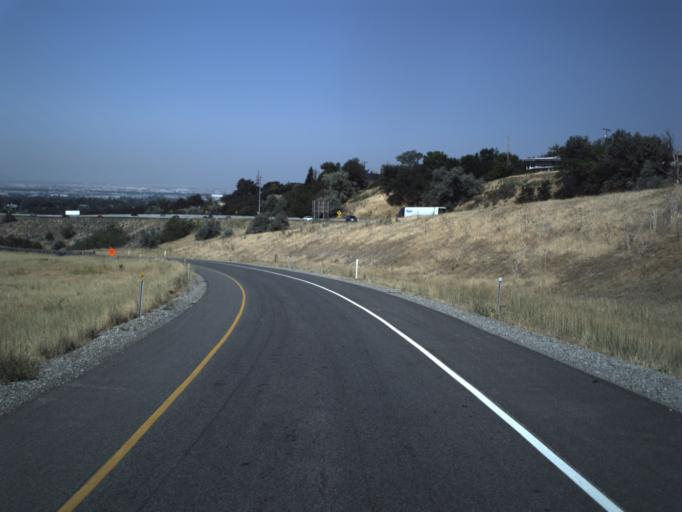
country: US
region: Utah
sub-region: Salt Lake County
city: East Millcreek
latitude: 40.7137
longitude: -111.8089
